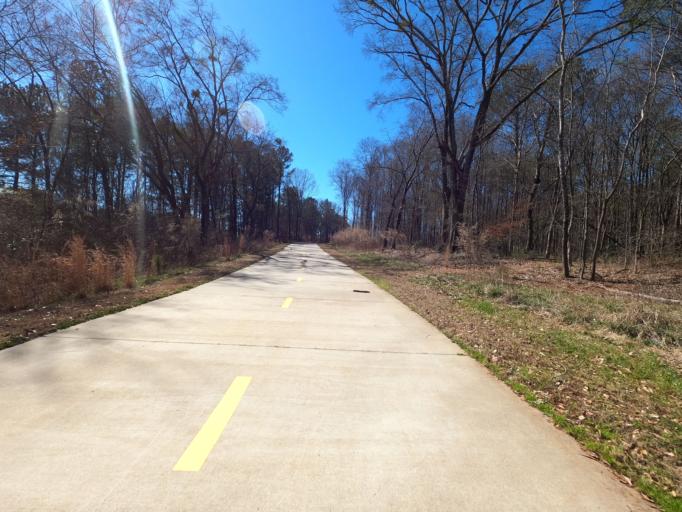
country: US
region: Georgia
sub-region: Clarke County
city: Athens
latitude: 33.9436
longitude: -83.3618
